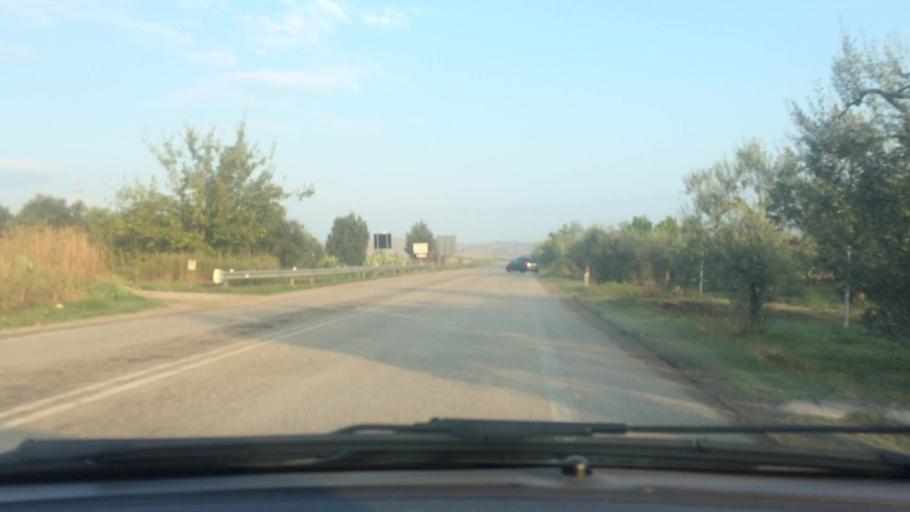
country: IT
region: Basilicate
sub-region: Provincia di Matera
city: Montescaglioso
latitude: 40.5271
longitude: 16.6249
